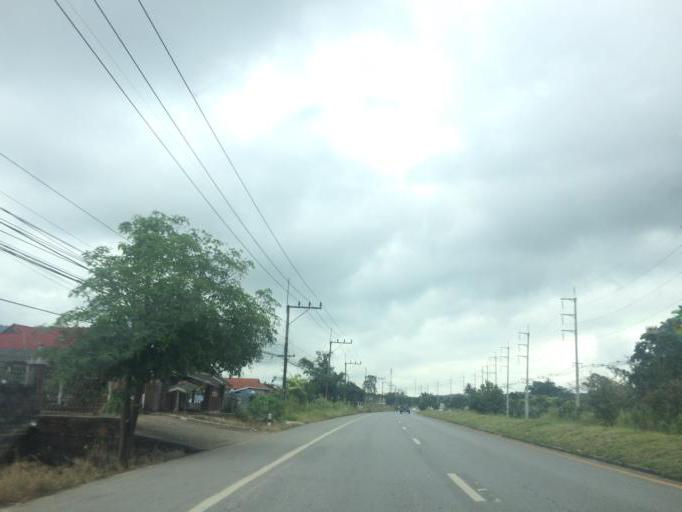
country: TH
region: Chiang Rai
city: Mae Chan
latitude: 20.0874
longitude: 99.8747
